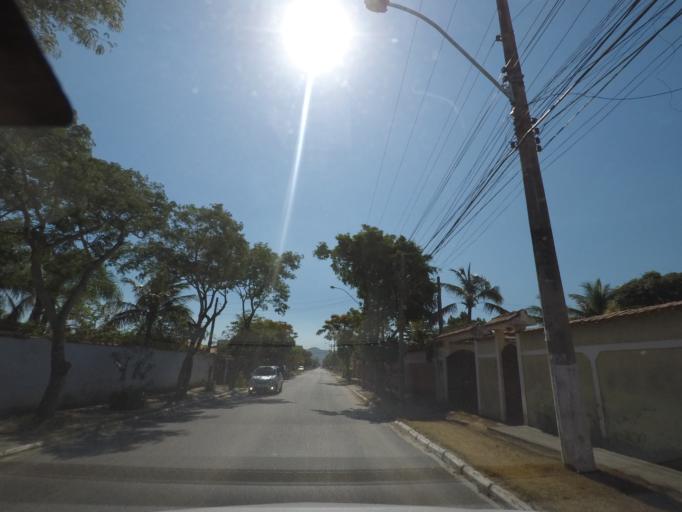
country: BR
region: Rio de Janeiro
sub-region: Marica
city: Marica
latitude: -22.9671
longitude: -42.9486
